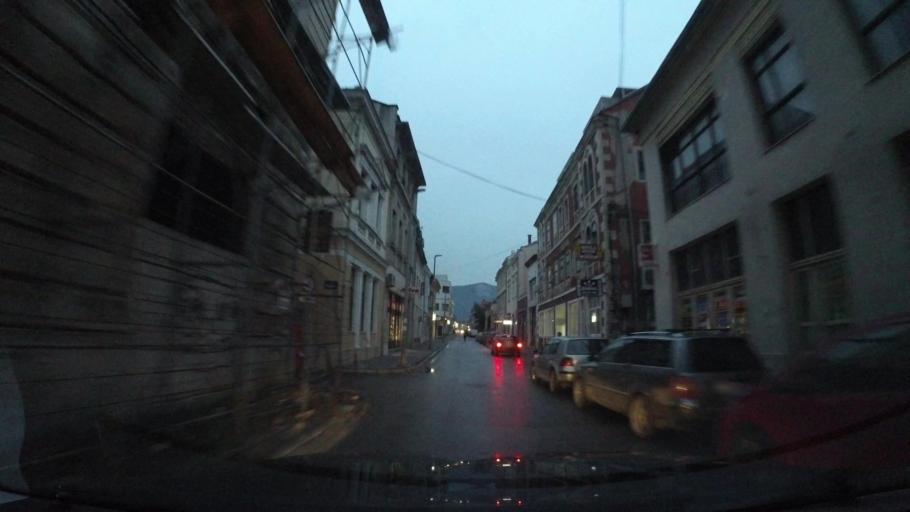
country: BA
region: Federation of Bosnia and Herzegovina
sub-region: Hercegovacko-Bosanski Kanton
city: Mostar
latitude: 43.3407
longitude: 17.8149
